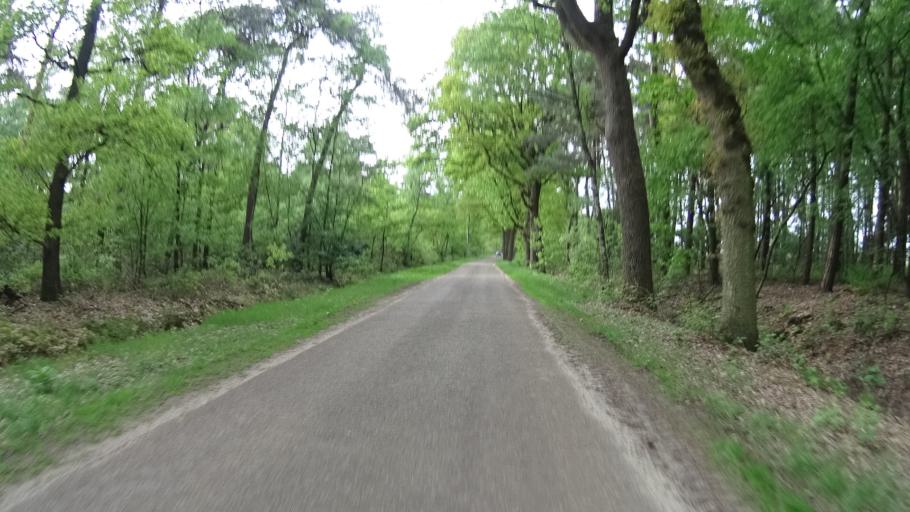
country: NL
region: North Brabant
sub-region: Gemeente Veghel
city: Erp
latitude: 51.6194
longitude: 5.6231
